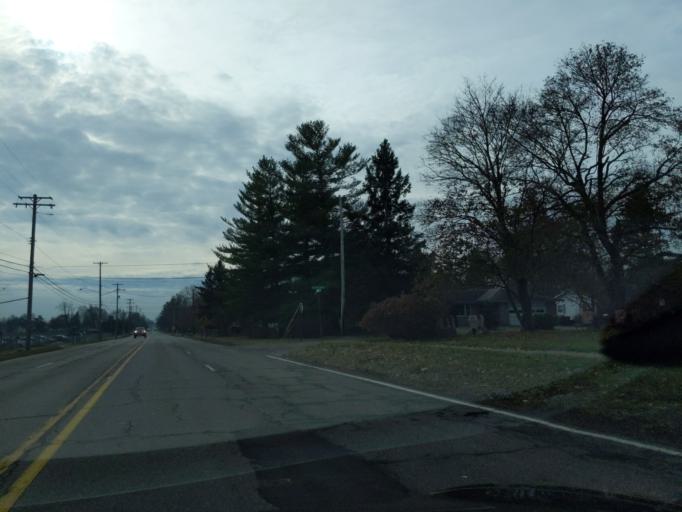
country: US
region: Michigan
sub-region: Ingham County
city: Holt
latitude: 42.6349
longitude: -84.5234
